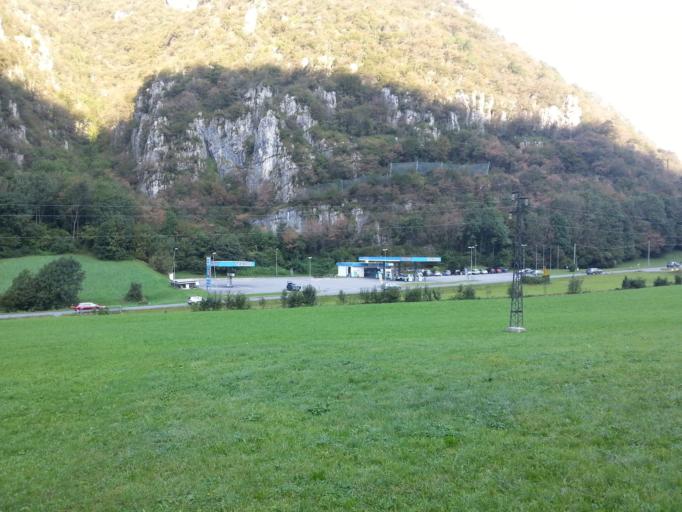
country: IT
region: Lombardy
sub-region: Provincia di Lecco
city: Ballabio
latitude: 45.9141
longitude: 9.4346
